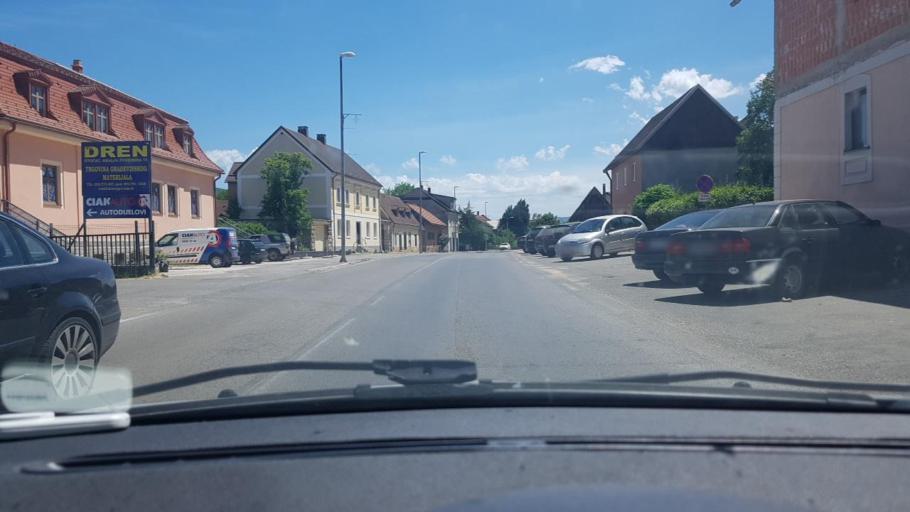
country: HR
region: Licko-Senjska
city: Otocac
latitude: 44.8694
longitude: 15.2419
